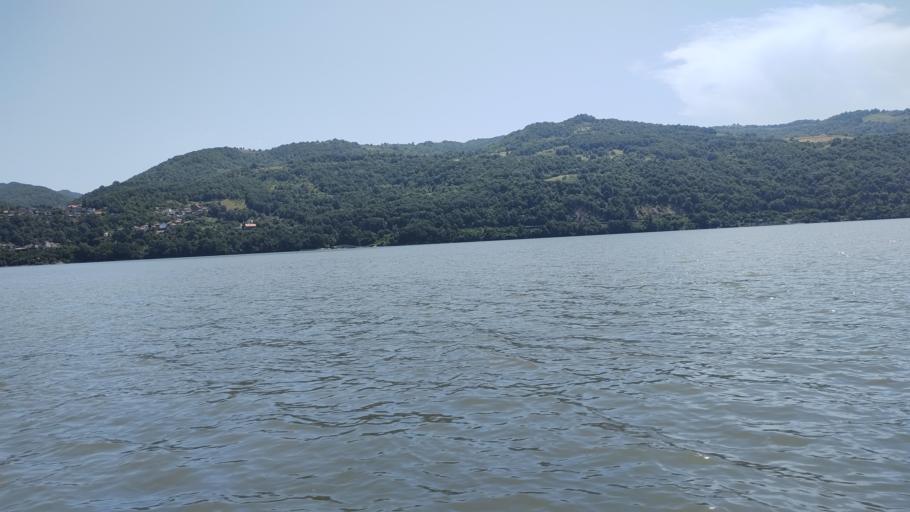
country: RO
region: Mehedinti
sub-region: Comuna Svinita
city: Svinita
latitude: 44.4956
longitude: 22.1877
